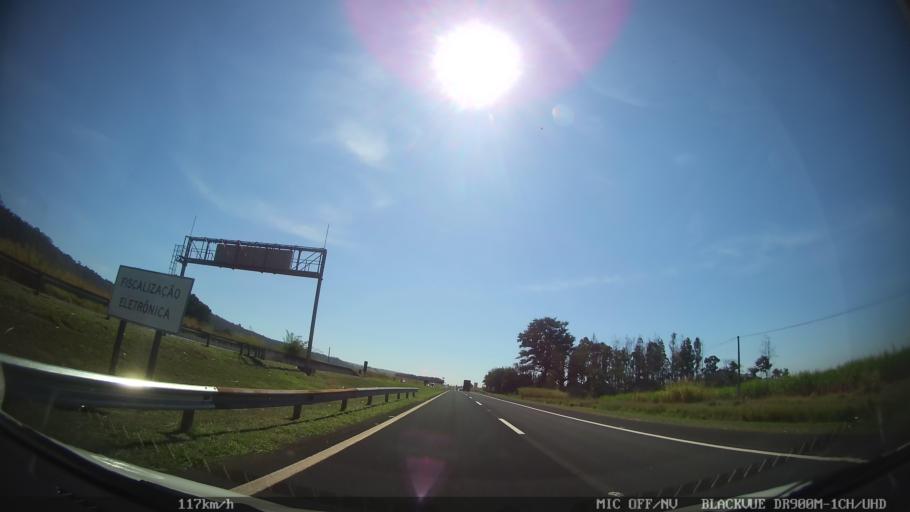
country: BR
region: Sao Paulo
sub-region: Sao Simao
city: Sao Simao
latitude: -21.5193
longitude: -47.6430
